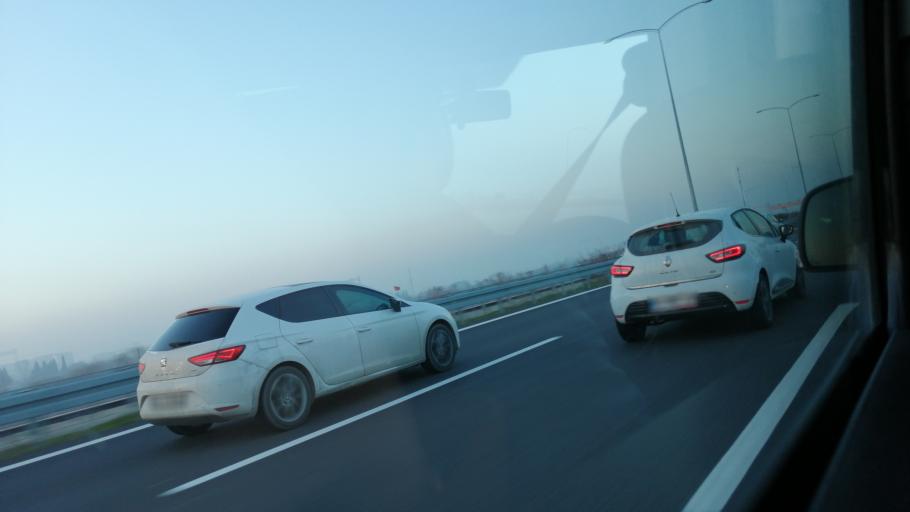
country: TR
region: Yalova
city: Altinova
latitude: 40.7127
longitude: 29.4981
